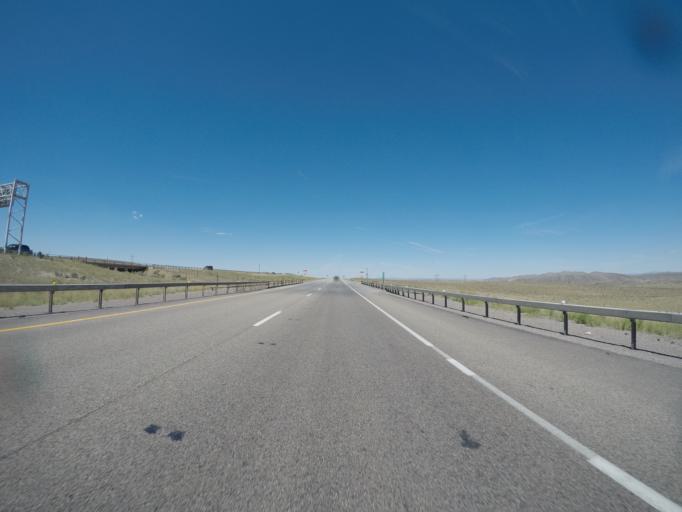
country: US
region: Wyoming
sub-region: Carbon County
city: Saratoga
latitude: 41.7420
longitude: -106.8426
